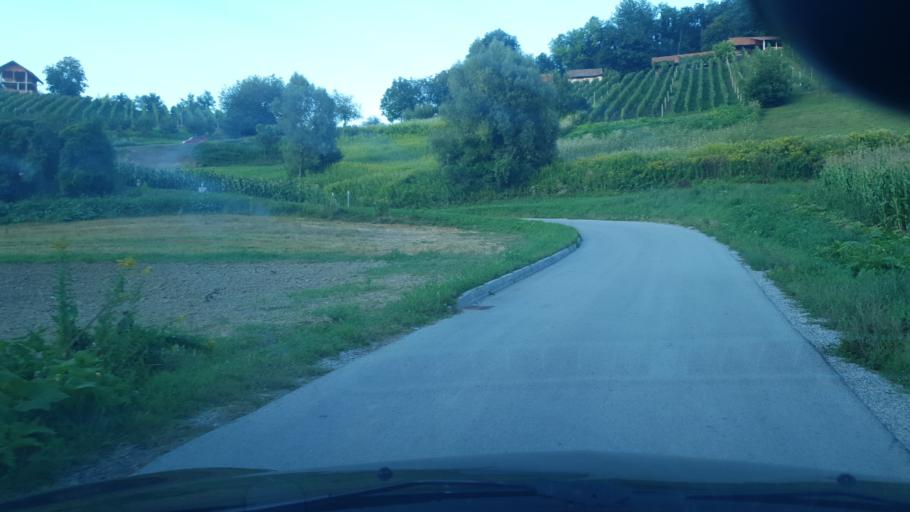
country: HR
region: Krapinsko-Zagorska
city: Zabok
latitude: 46.0606
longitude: 15.8909
